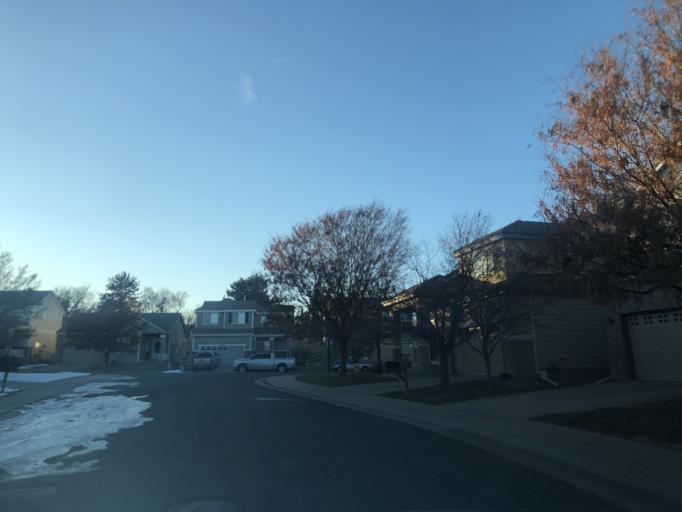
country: US
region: Colorado
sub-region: Adams County
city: Aurora
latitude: 39.7154
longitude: -104.8119
